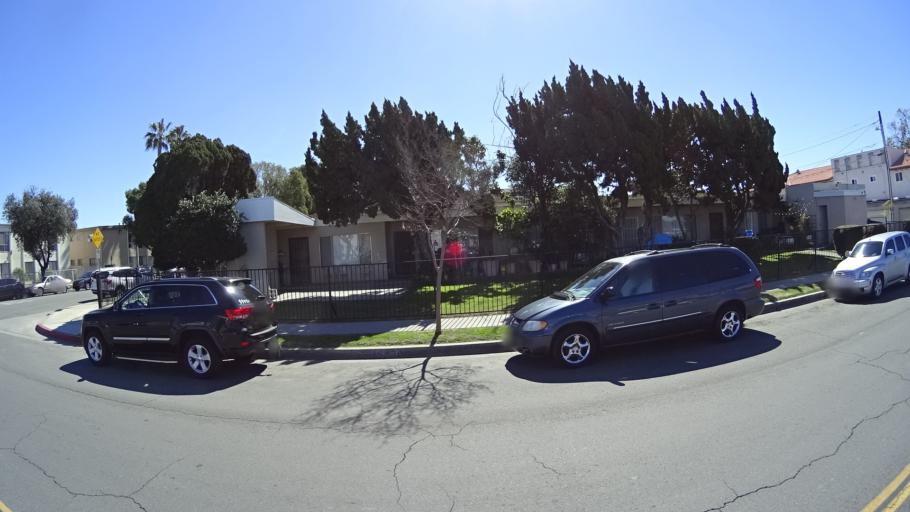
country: US
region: California
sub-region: Orange County
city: Anaheim
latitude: 33.8211
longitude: -117.9188
